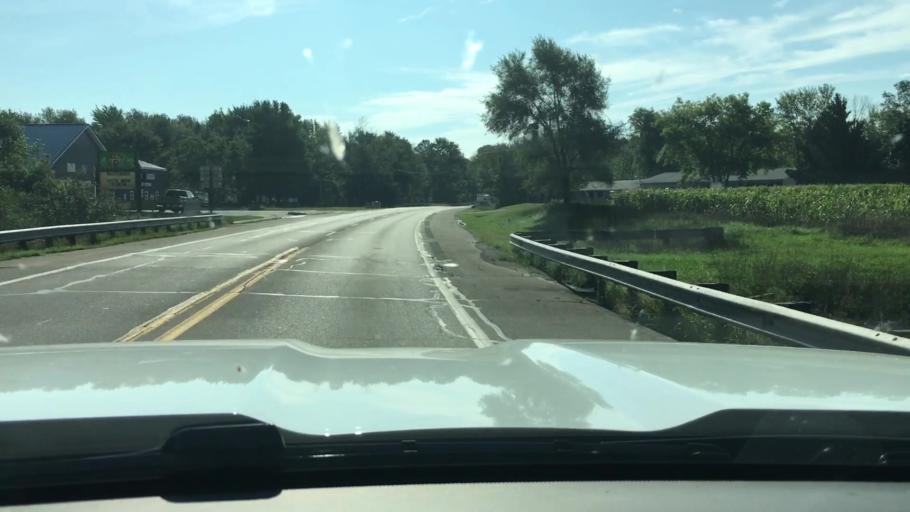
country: US
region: Michigan
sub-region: Montcalm County
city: Edmore
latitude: 43.4260
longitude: -85.1474
